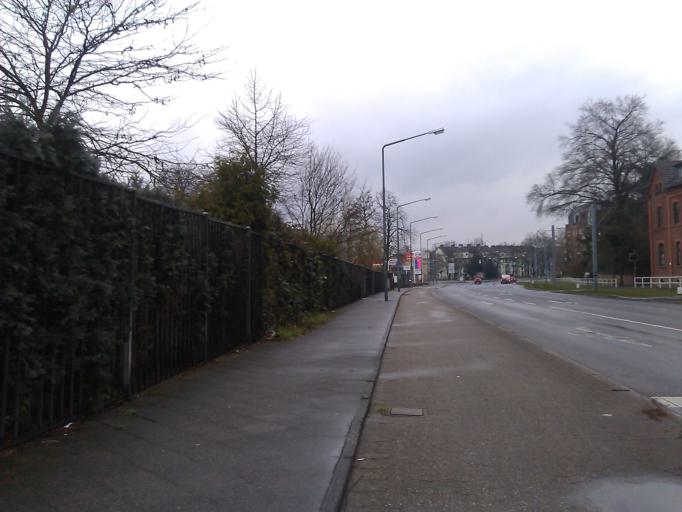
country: DE
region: North Rhine-Westphalia
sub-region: Regierungsbezirk Dusseldorf
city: Ratingen
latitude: 51.2882
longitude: 6.8400
